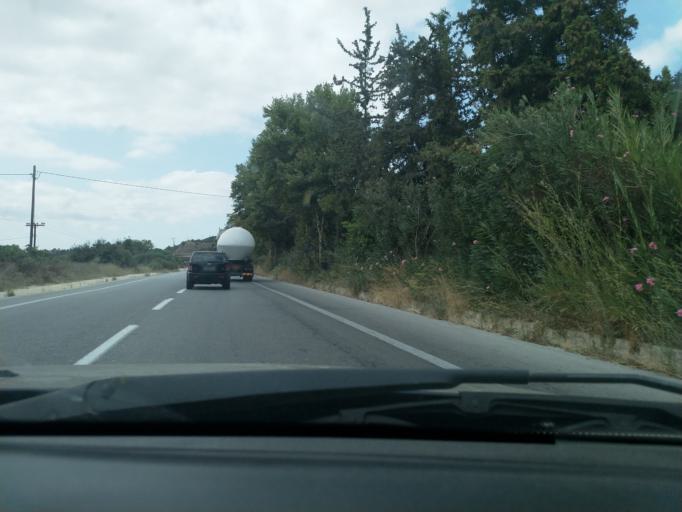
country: GR
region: Crete
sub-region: Nomos Chanias
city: Georgioupolis
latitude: 35.3744
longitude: 24.2098
